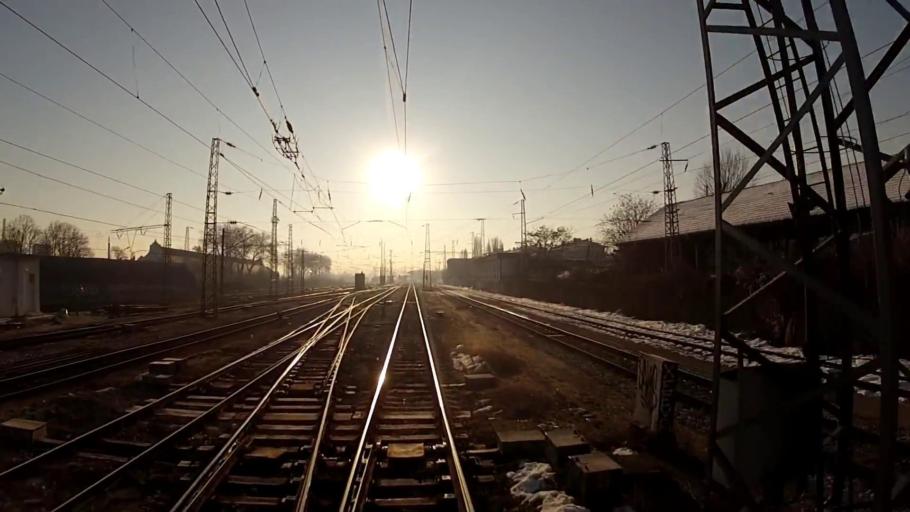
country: BG
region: Sofia-Capital
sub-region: Stolichna Obshtina
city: Sofia
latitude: 42.7233
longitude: 23.2941
